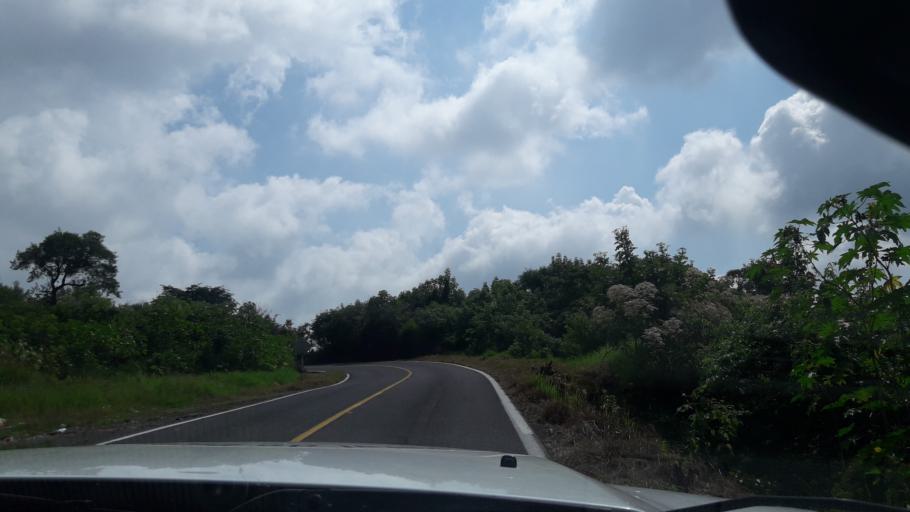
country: MX
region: Colima
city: Suchitlan
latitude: 19.4365
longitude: -103.7090
